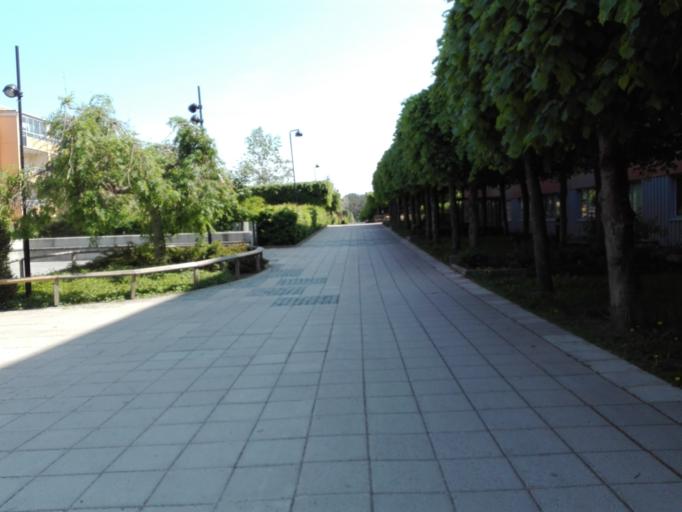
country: SE
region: Stockholm
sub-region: Nacka Kommun
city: Fisksatra
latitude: 59.2921
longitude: 18.2519
